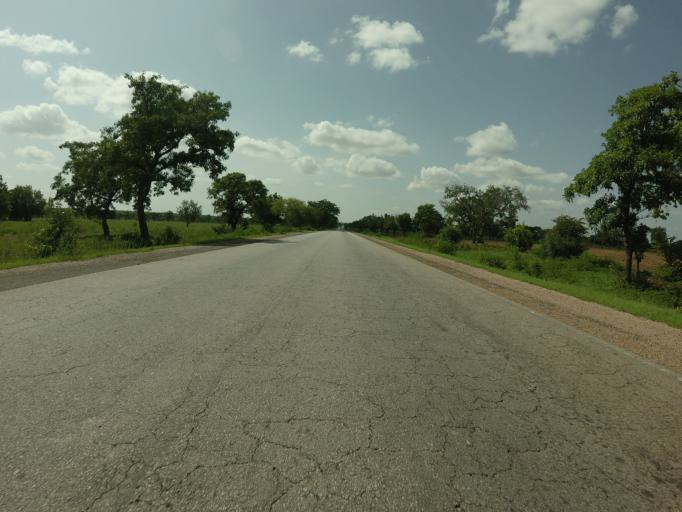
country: GH
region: Northern
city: Savelugu
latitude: 9.8202
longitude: -0.8631
